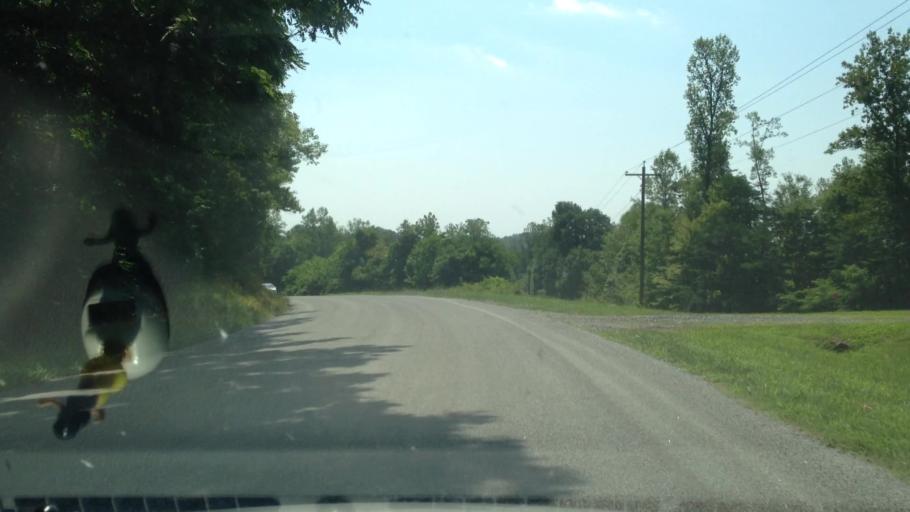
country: US
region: Virginia
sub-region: Patrick County
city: Stuart
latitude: 36.5941
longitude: -80.2926
